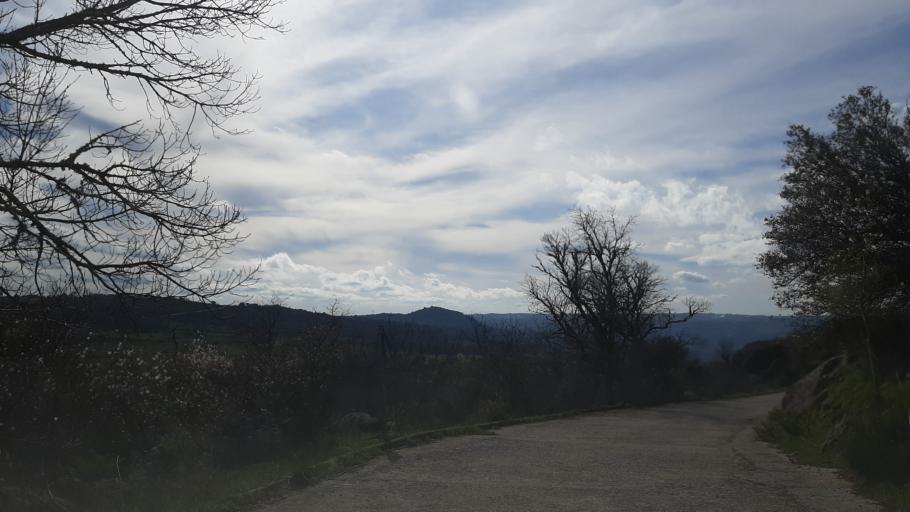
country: ES
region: Castille and Leon
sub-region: Provincia de Salamanca
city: Villarino de los Aires
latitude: 41.2624
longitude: -6.5261
